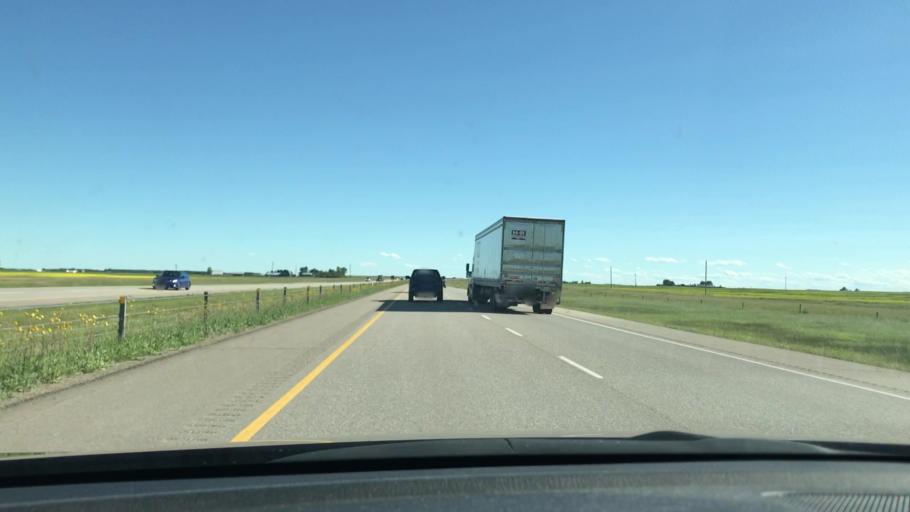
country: CA
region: Alberta
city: Didsbury
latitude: 51.6833
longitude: -114.0256
